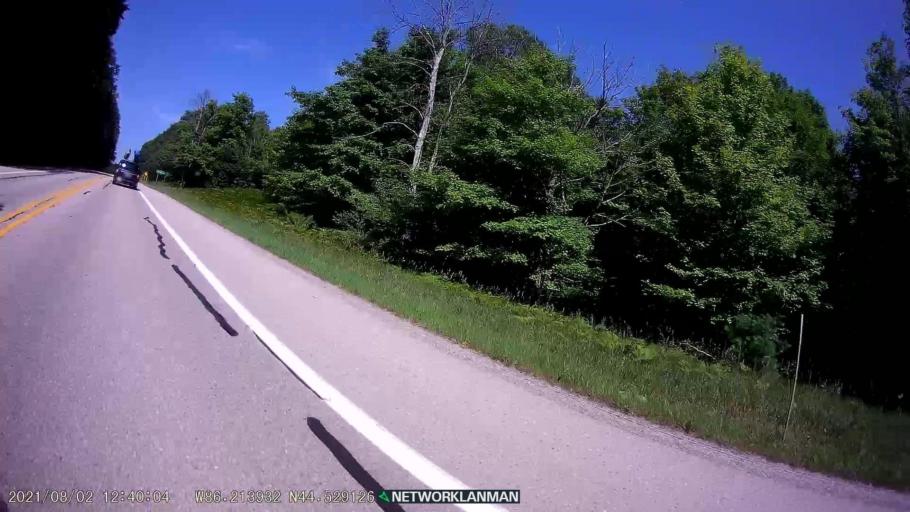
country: US
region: Michigan
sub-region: Benzie County
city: Frankfort
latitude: 44.5294
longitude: -86.2138
